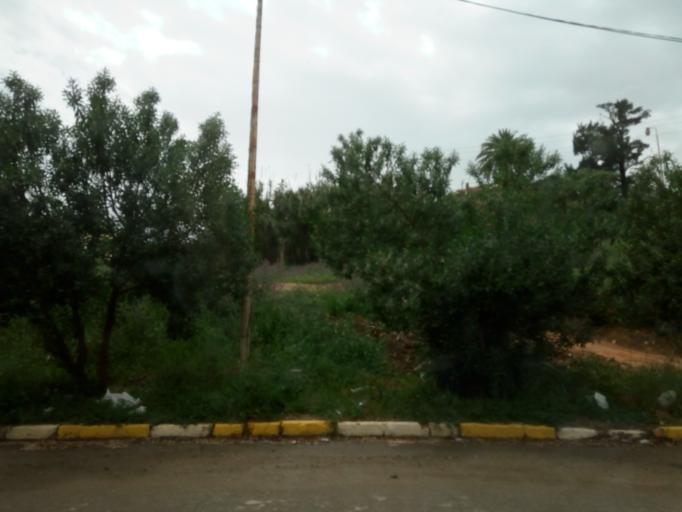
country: DZ
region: Tipaza
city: Douera
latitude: 36.6877
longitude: 2.9655
